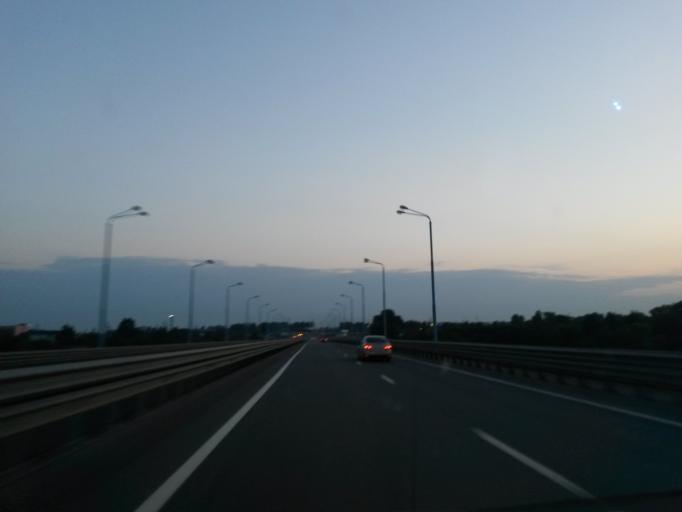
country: RU
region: Jaroslavl
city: Yaroslavl
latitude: 57.6732
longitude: 39.8524
